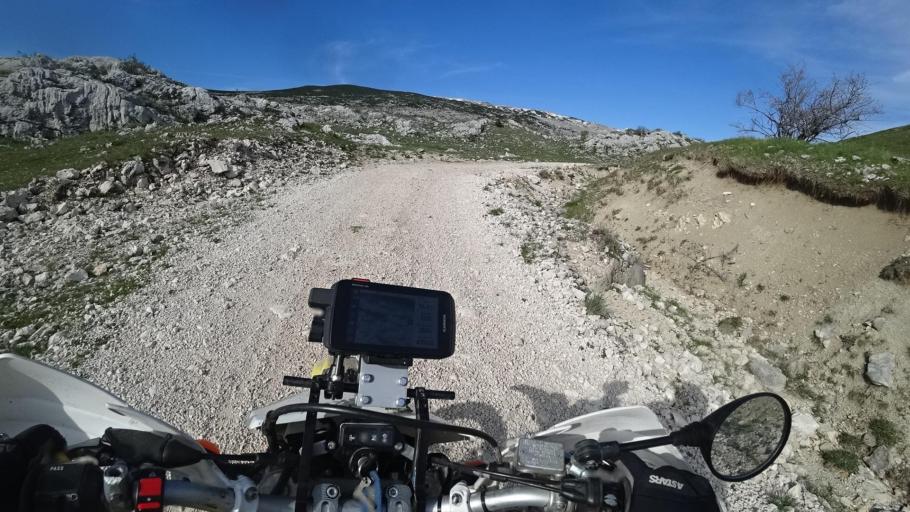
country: BA
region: Federation of Bosnia and Herzegovina
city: Kocerin
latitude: 43.5769
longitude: 17.5131
